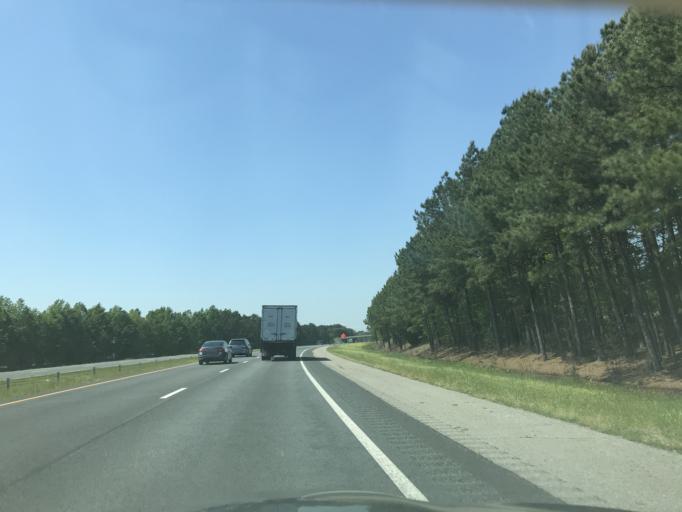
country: US
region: North Carolina
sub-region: Johnston County
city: Benson
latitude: 35.3717
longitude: -78.5000
